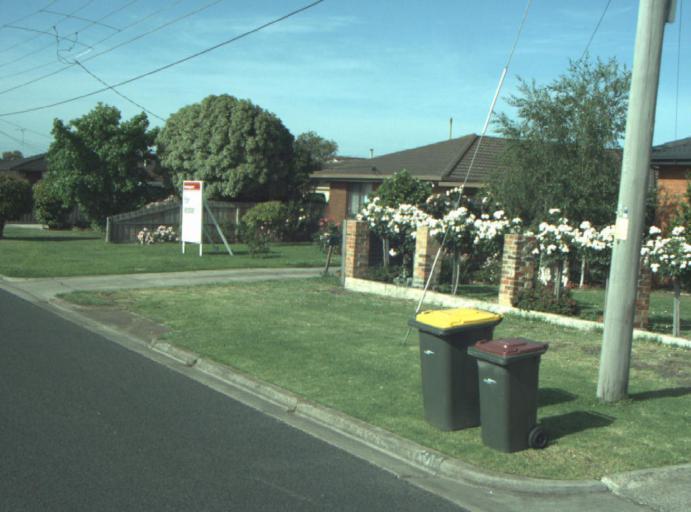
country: AU
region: Victoria
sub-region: Greater Geelong
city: Hamlyn Heights
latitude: -38.1192
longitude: 144.3218
